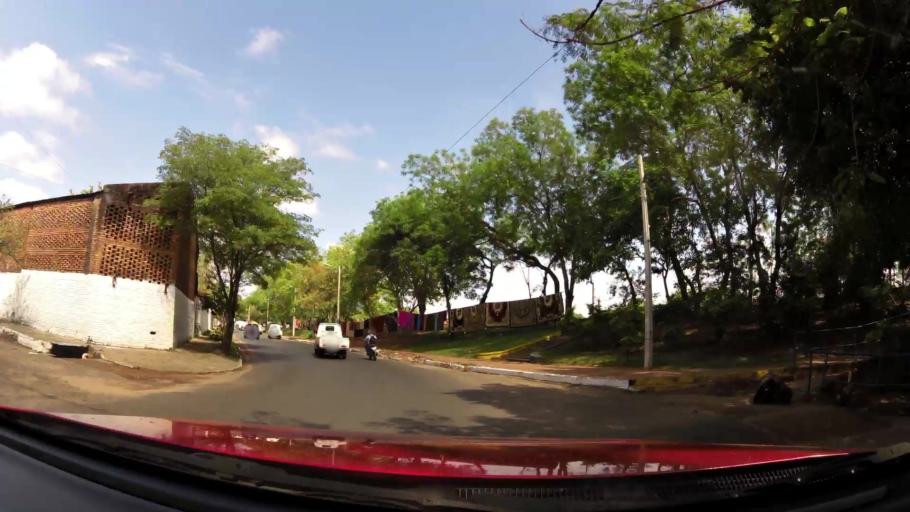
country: PY
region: Central
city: San Lorenzo
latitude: -25.2648
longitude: -57.4973
